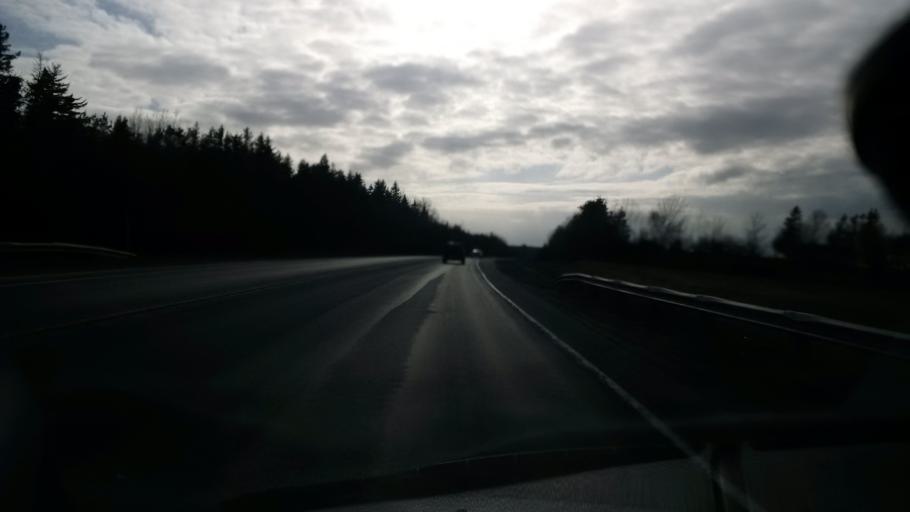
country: CA
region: Nova Scotia
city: New Glasgow
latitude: 45.5729
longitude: -62.3759
